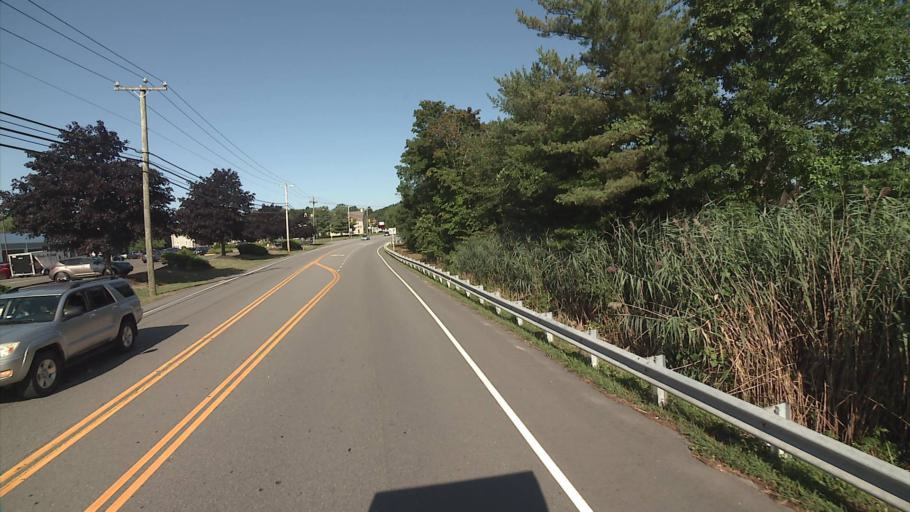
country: US
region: Connecticut
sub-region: Middlesex County
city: Clinton
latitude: 41.2711
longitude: -72.5009
